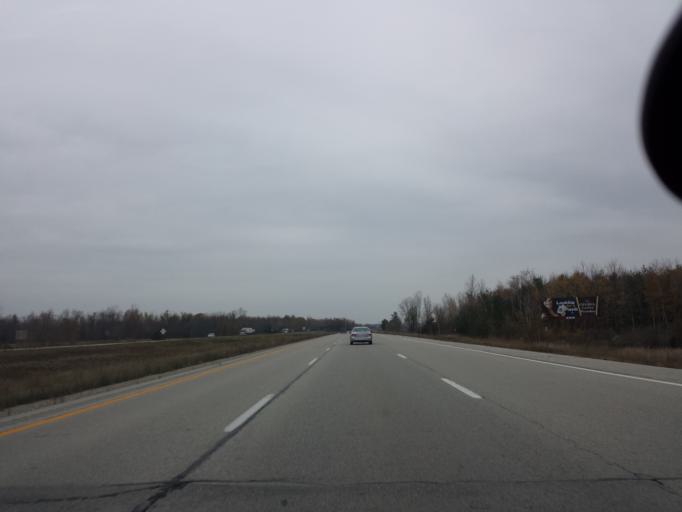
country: US
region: Michigan
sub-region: Arenac County
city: Standish
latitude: 43.9535
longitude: -84.0146
